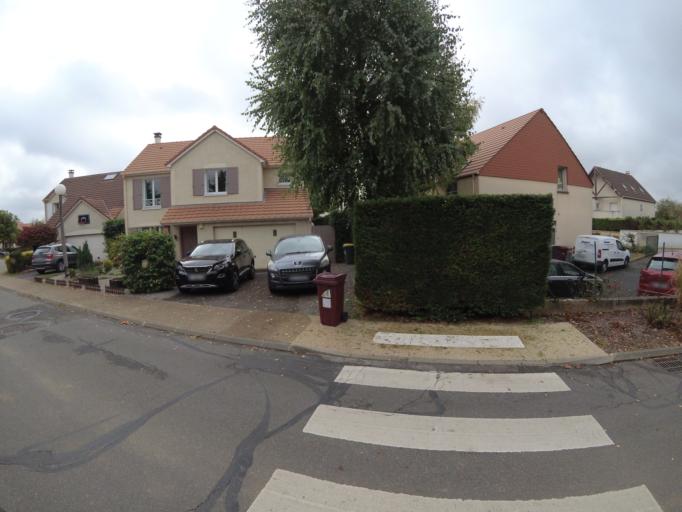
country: FR
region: Ile-de-France
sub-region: Departement de Seine-et-Marne
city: Montevrain
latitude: 48.8752
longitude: 2.7529
